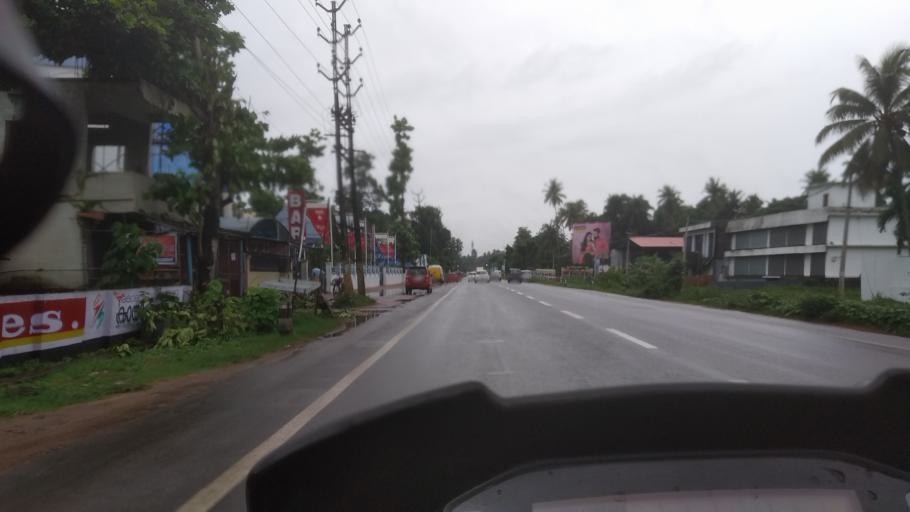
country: IN
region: Kerala
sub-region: Alappuzha
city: Kayankulam
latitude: 9.1305
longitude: 76.5149
